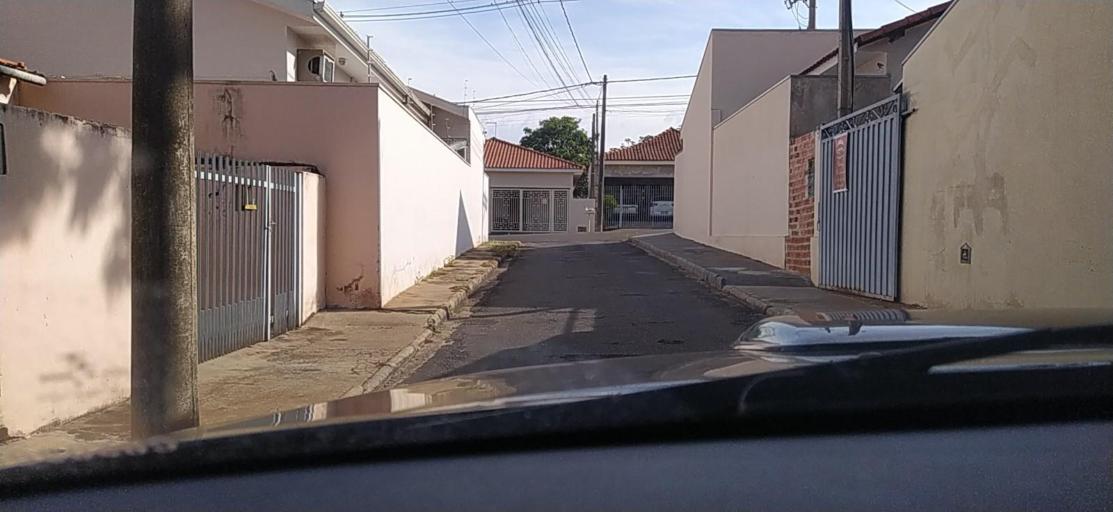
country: BR
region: Sao Paulo
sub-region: Pindorama
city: Pindorama
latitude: -21.1906
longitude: -48.9034
